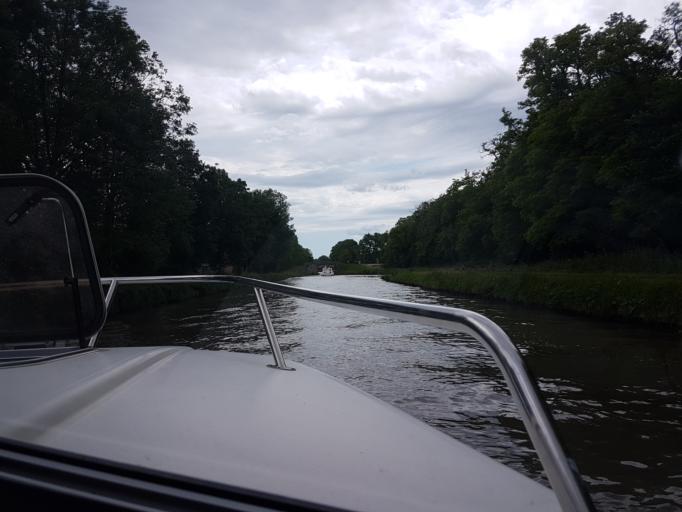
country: FR
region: Bourgogne
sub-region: Departement de la Nievre
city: Clamecy
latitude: 47.4845
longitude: 3.5242
